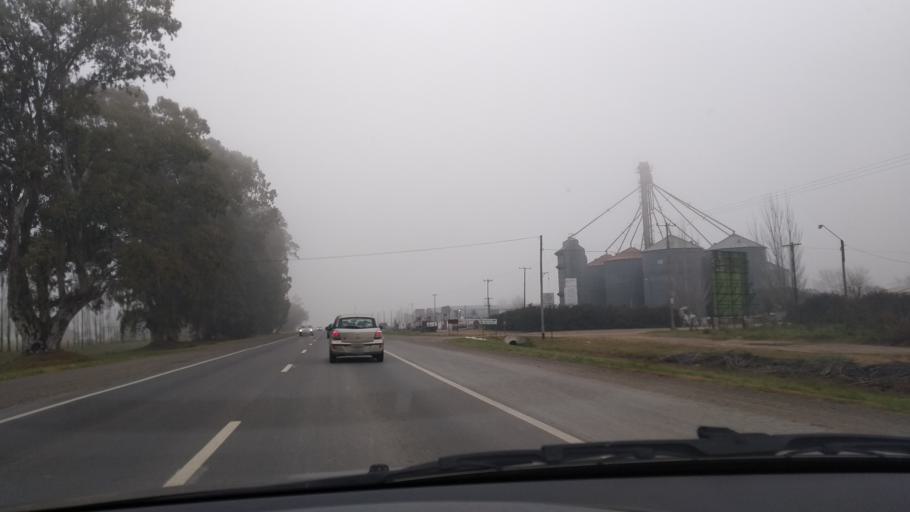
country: AR
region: Buenos Aires
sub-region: Partido de Azul
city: Azul
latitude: -36.8054
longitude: -59.8563
